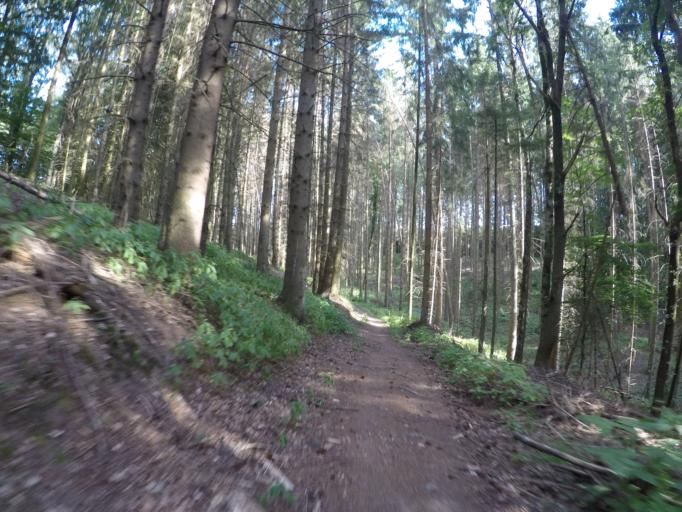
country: LU
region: Luxembourg
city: Itzig
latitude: 49.6006
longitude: 6.1688
